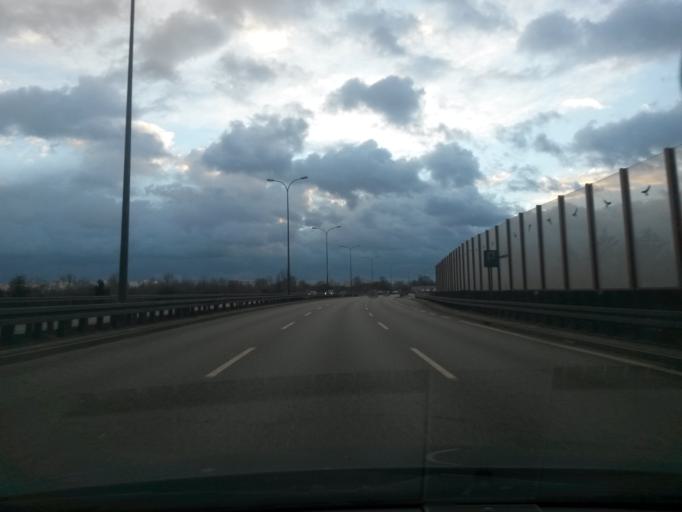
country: PL
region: Masovian Voivodeship
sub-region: Warszawa
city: Praga Poludnie
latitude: 52.2065
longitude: 21.0828
